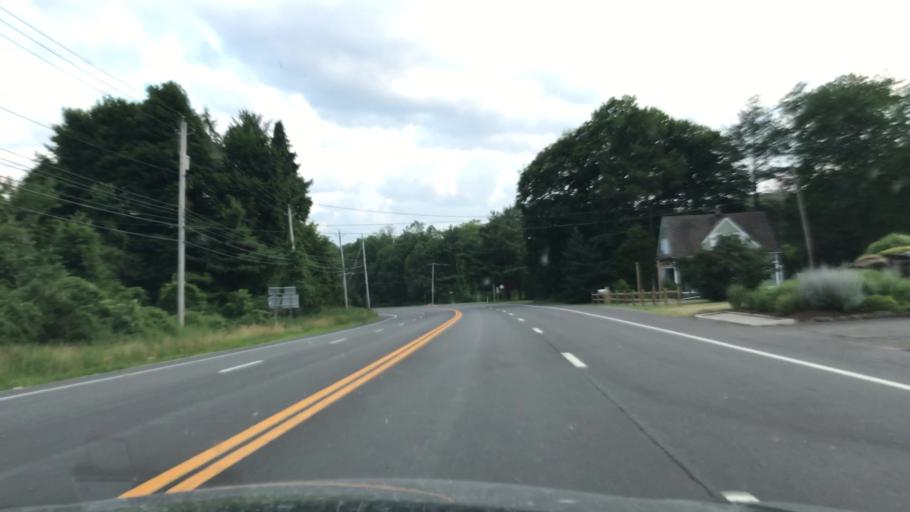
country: US
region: New York
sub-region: Rockland County
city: Sloatsburg
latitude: 41.2254
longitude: -74.1872
